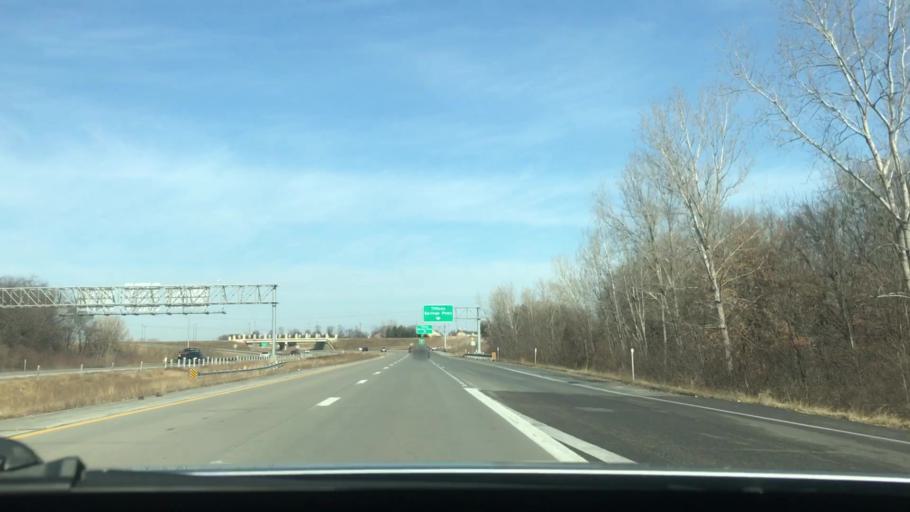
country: US
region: Missouri
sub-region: Clay County
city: Gladstone
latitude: 39.2648
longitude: -94.5857
